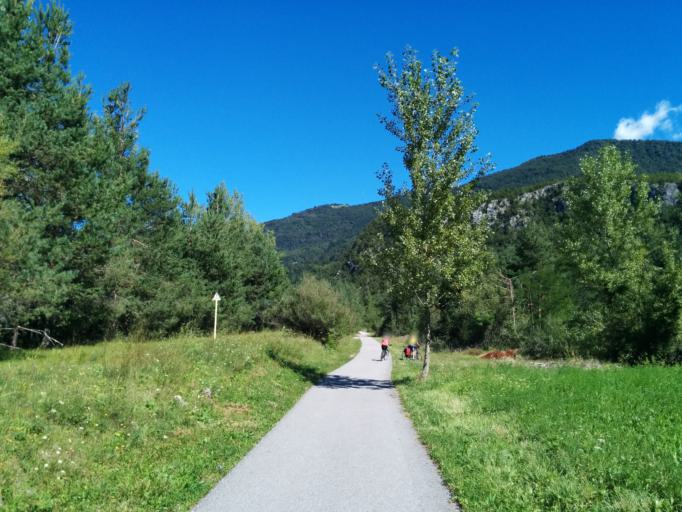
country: IT
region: Friuli Venezia Giulia
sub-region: Provincia di Udine
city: Villa Santina
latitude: 46.4178
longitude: 12.9072
